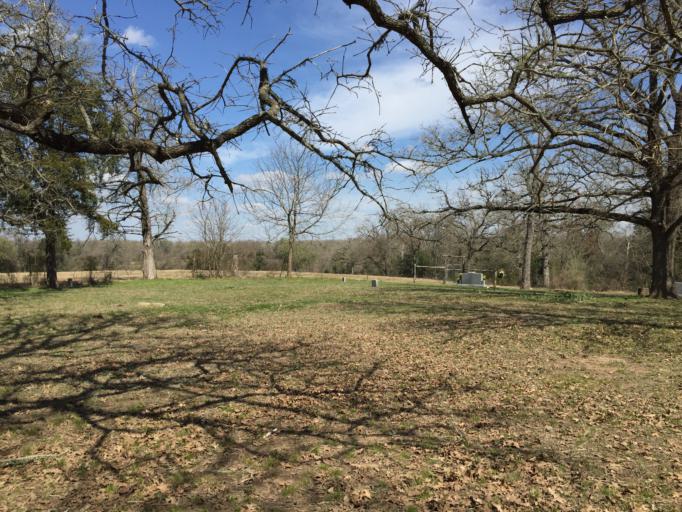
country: US
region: Texas
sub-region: Milam County
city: Thorndale
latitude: 30.5598
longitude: -97.1753
